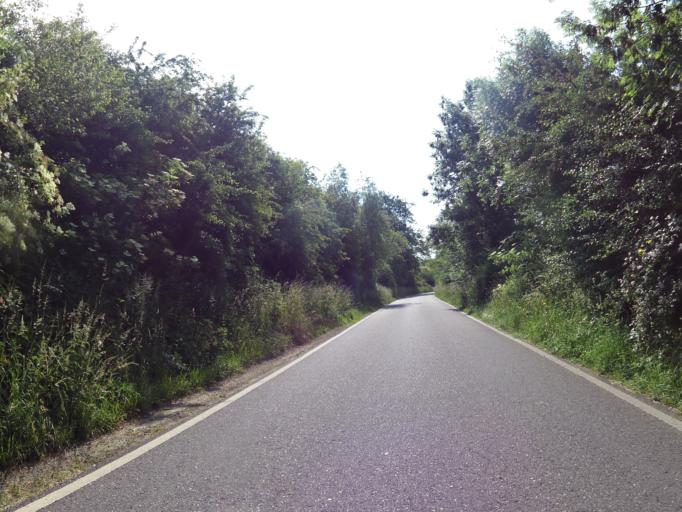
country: NL
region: Limburg
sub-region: Gemeente Vaals
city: Vaals
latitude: 50.7844
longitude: 6.0037
